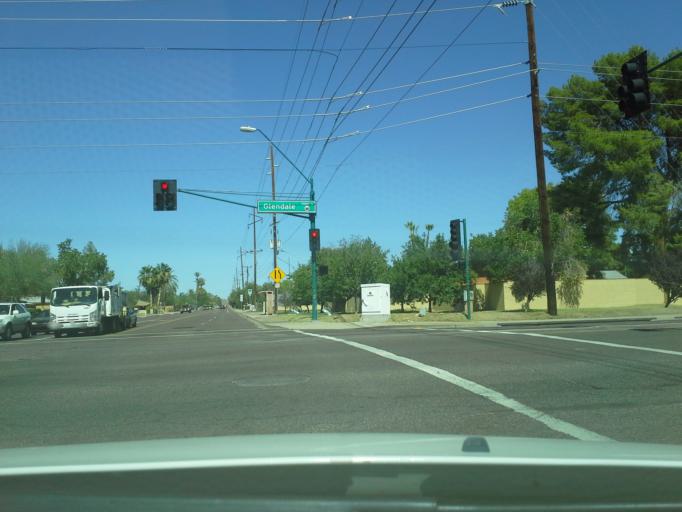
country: US
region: Arizona
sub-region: Maricopa County
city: Phoenix
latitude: 33.5381
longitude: -112.0562
